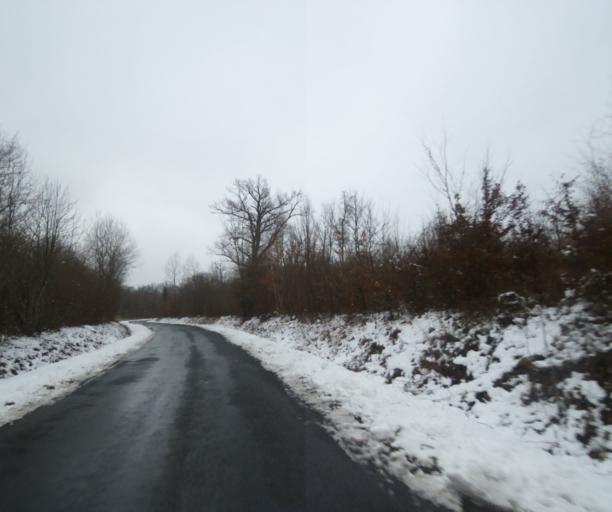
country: FR
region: Champagne-Ardenne
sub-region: Departement de la Haute-Marne
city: Laneuville-a-Remy
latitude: 48.4857
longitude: 4.8673
